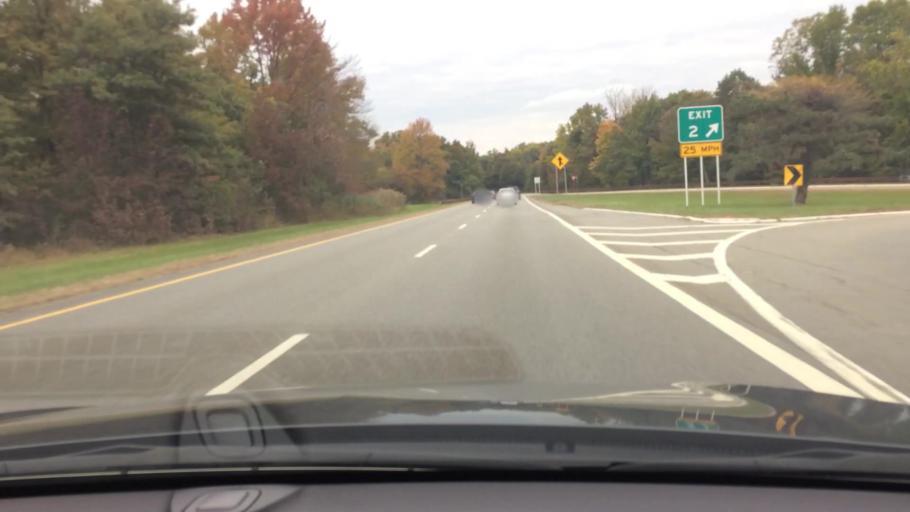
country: US
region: New Jersey
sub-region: Bergen County
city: Alpine
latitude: 40.9561
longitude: -73.9202
